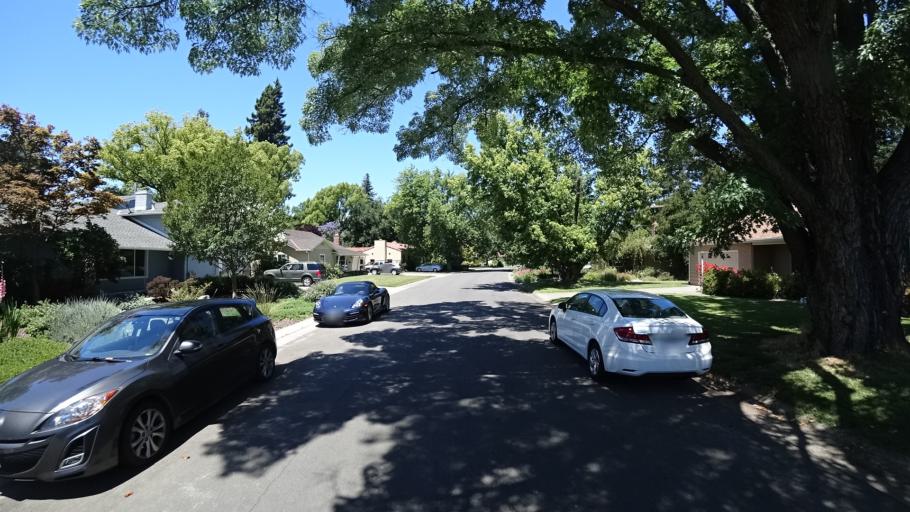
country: US
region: California
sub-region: Yolo County
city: West Sacramento
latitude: 38.5293
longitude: -121.5231
